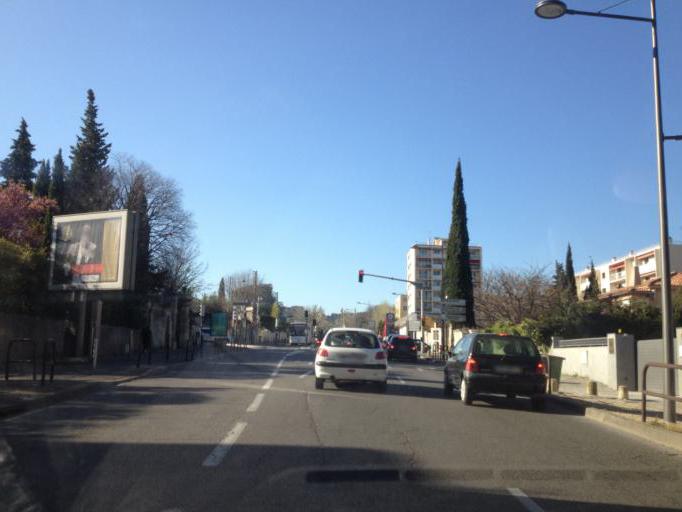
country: FR
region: Provence-Alpes-Cote d'Azur
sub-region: Departement des Bouches-du-Rhone
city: Aix-en-Provence
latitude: 43.5316
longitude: 5.4377
